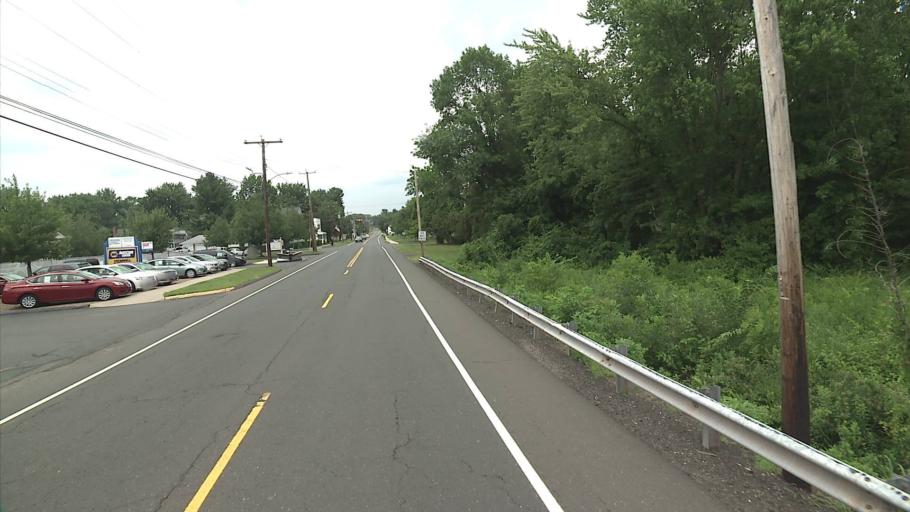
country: US
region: Connecticut
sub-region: Middlesex County
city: Cromwell
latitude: 41.5904
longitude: -72.6464
